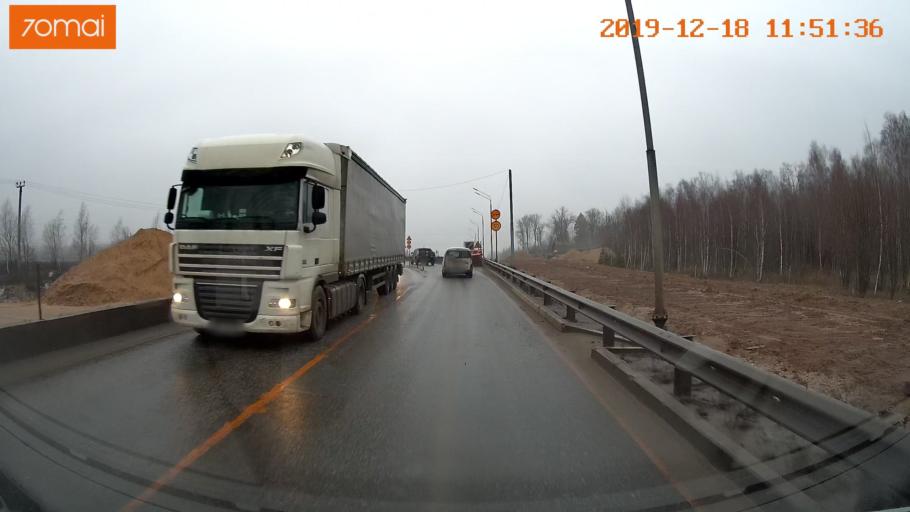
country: RU
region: Moskovskaya
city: Yershovo
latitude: 55.7945
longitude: 36.9217
